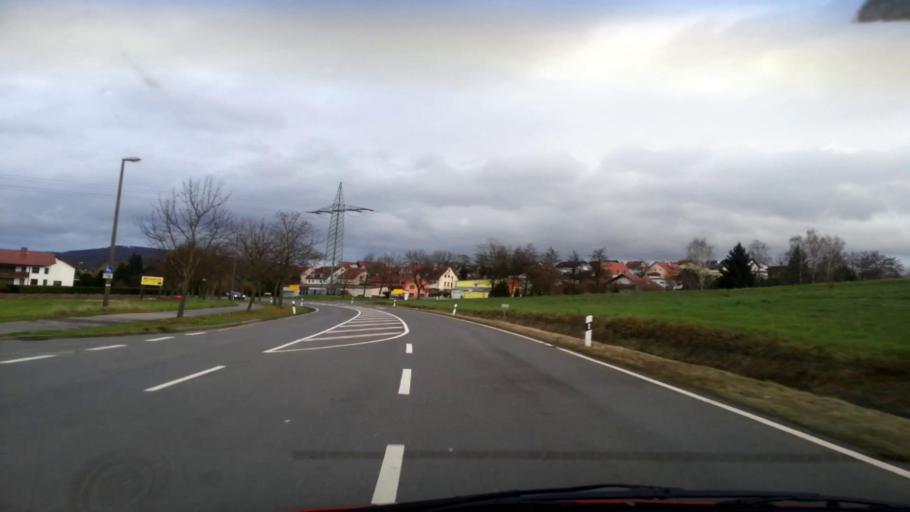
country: DE
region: Bavaria
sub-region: Upper Franconia
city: Litzendorf
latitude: 49.9096
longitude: 10.9970
